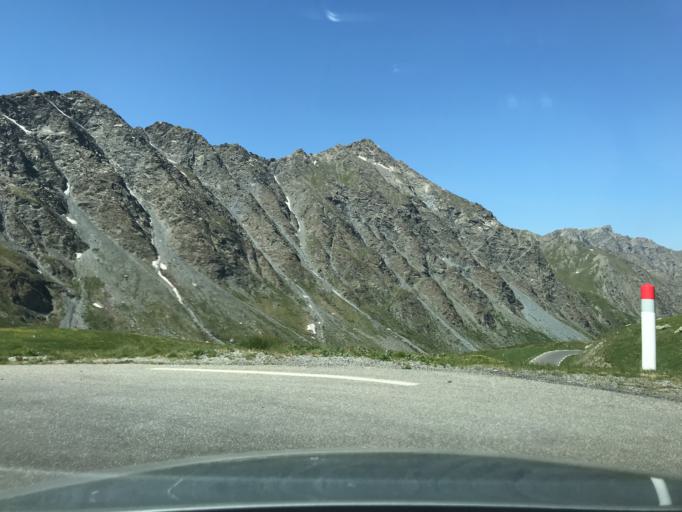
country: IT
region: Piedmont
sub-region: Provincia di Cuneo
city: Pontechianale
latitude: 44.6919
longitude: 6.9710
